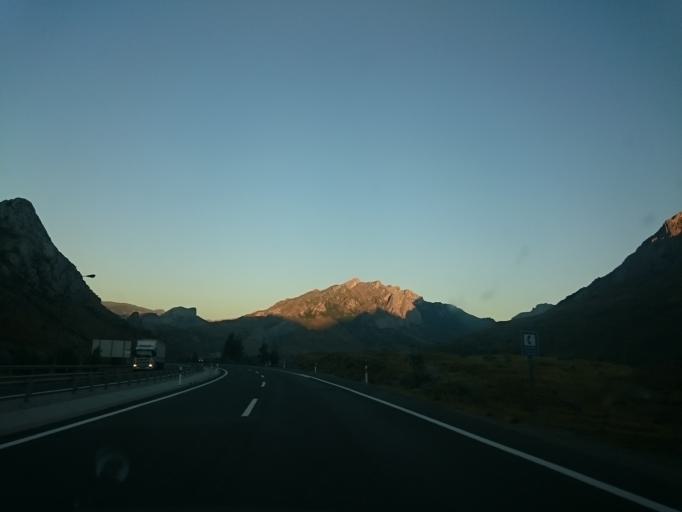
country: ES
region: Castille and Leon
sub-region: Provincia de Leon
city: Sena de Luna
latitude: 42.9281
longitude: -5.8608
